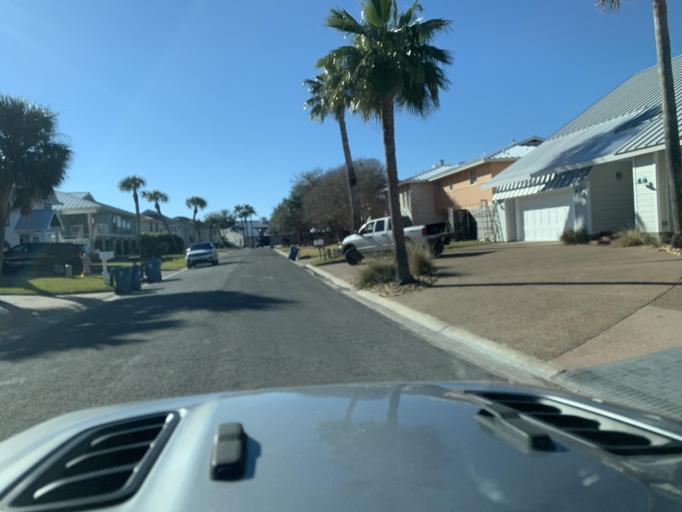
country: US
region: Texas
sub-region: Aransas County
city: Fulton
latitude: 28.0361
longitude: -97.0314
